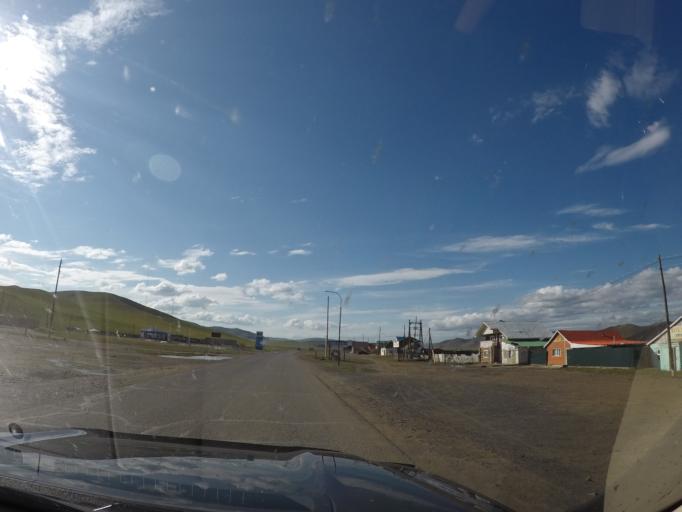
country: MN
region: Hentiy
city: Modot
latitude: 47.7238
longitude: 109.0264
